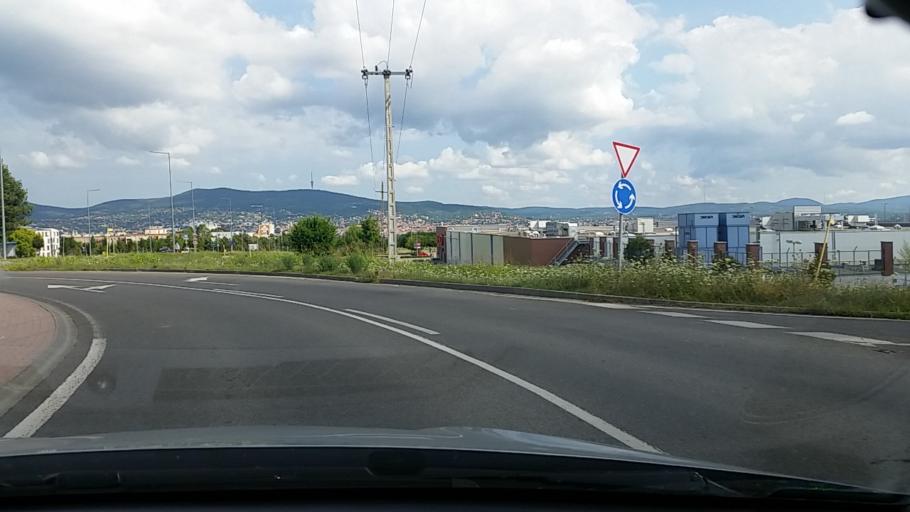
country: HU
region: Baranya
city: Pecs
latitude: 46.0358
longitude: 18.2333
